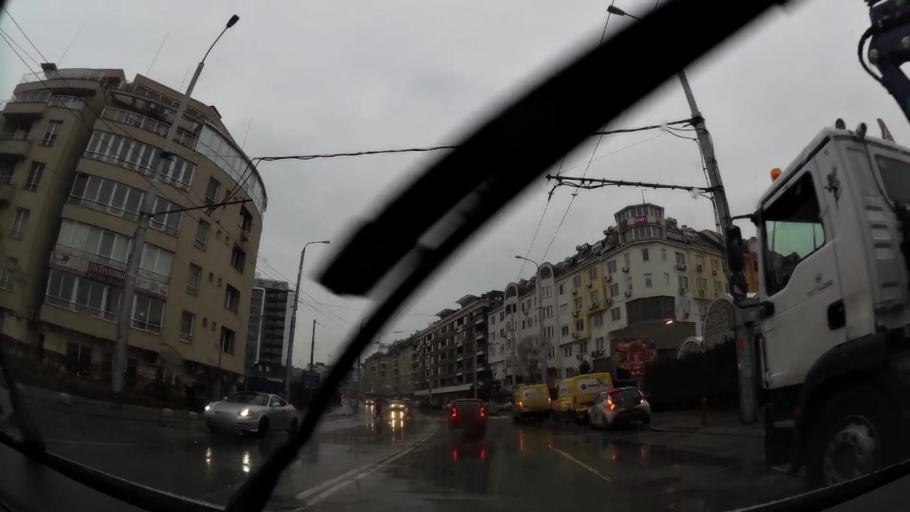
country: BG
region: Sofia-Capital
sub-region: Stolichna Obshtina
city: Sofia
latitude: 42.6554
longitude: 23.3742
